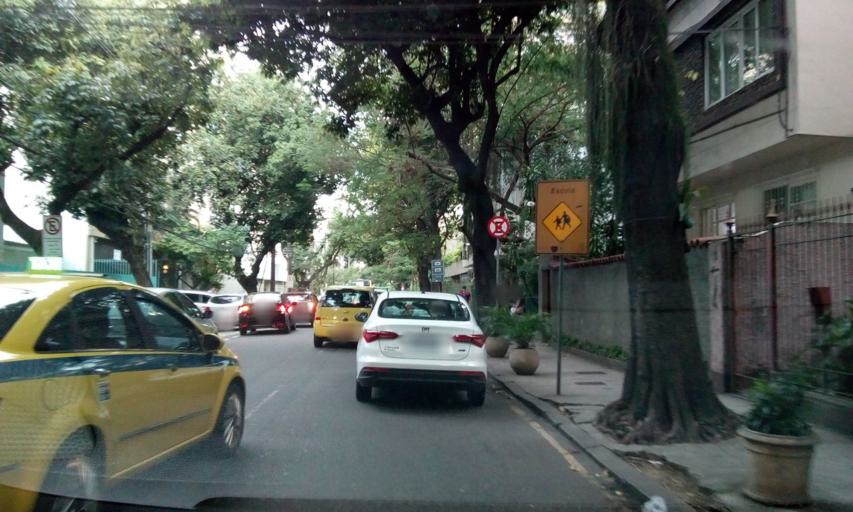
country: BR
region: Rio de Janeiro
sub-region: Rio De Janeiro
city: Rio de Janeiro
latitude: -22.9760
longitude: -43.2282
